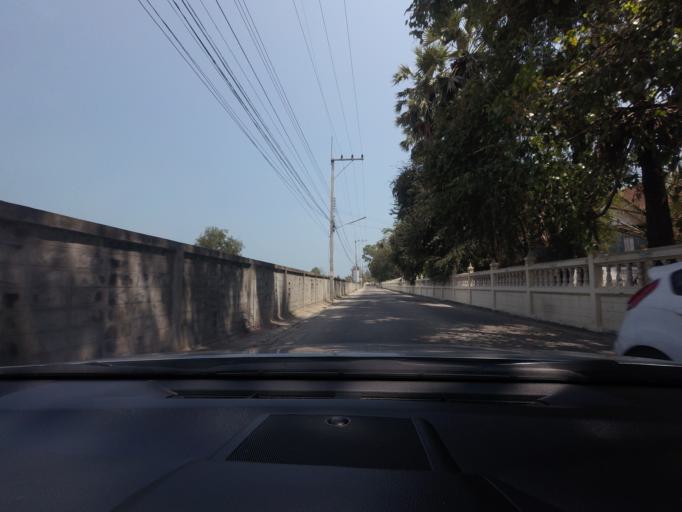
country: TH
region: Phetchaburi
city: Cha-am
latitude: 12.8149
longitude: 99.9905
